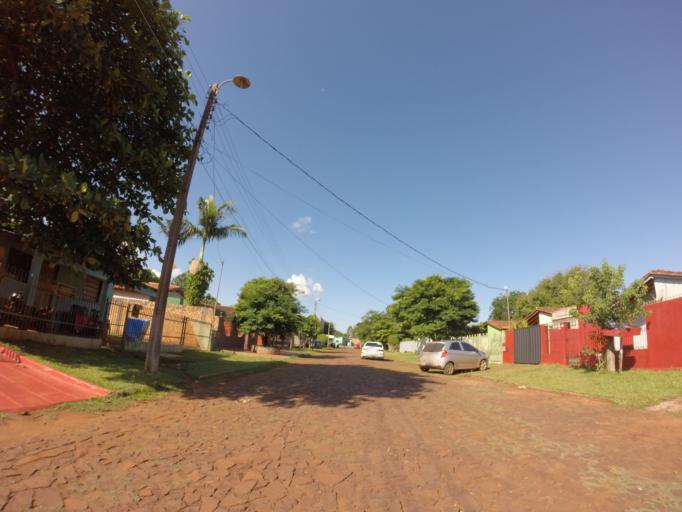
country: PY
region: Alto Parana
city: Ciudad del Este
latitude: -25.3747
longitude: -54.6497
